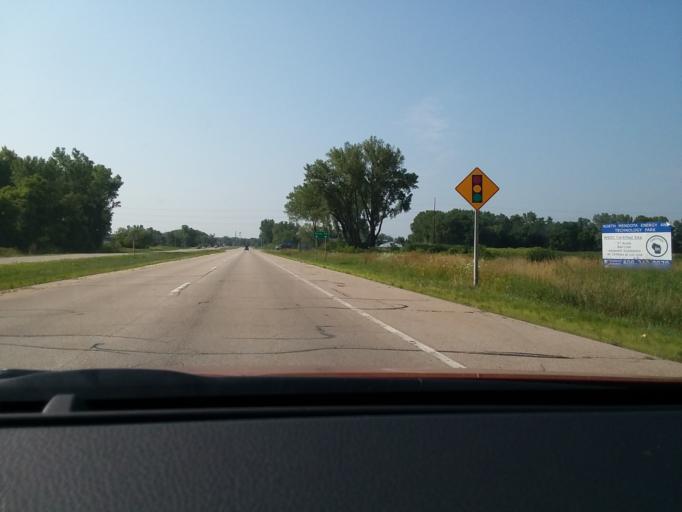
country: US
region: Wisconsin
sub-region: Dane County
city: Maple Bluff
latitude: 43.1619
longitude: -89.4062
